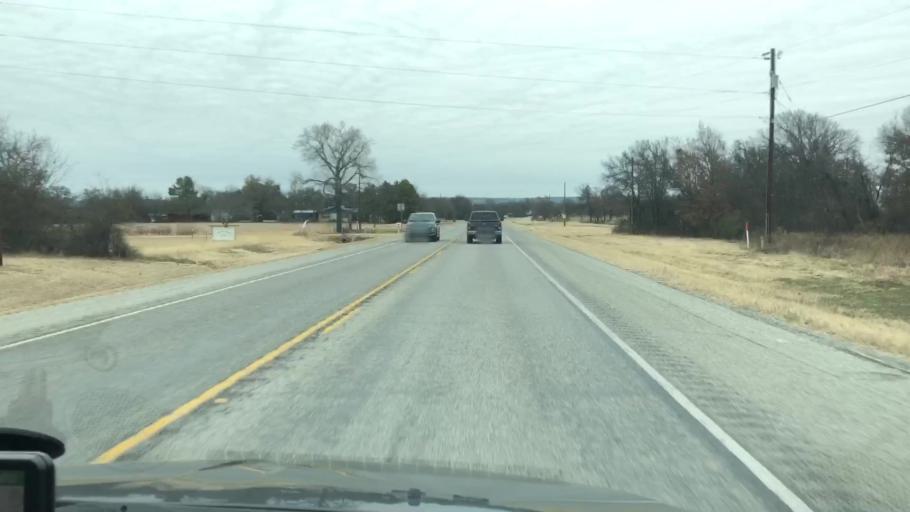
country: US
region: Texas
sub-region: Palo Pinto County
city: Mineral Wells
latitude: 32.8871
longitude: -98.0885
